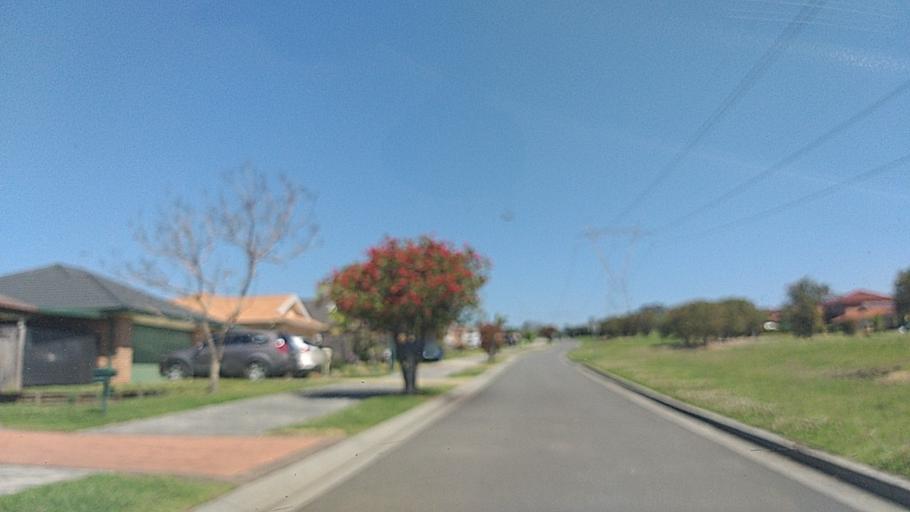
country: AU
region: New South Wales
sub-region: Wollongong
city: Dapto
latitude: -34.4882
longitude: 150.7688
